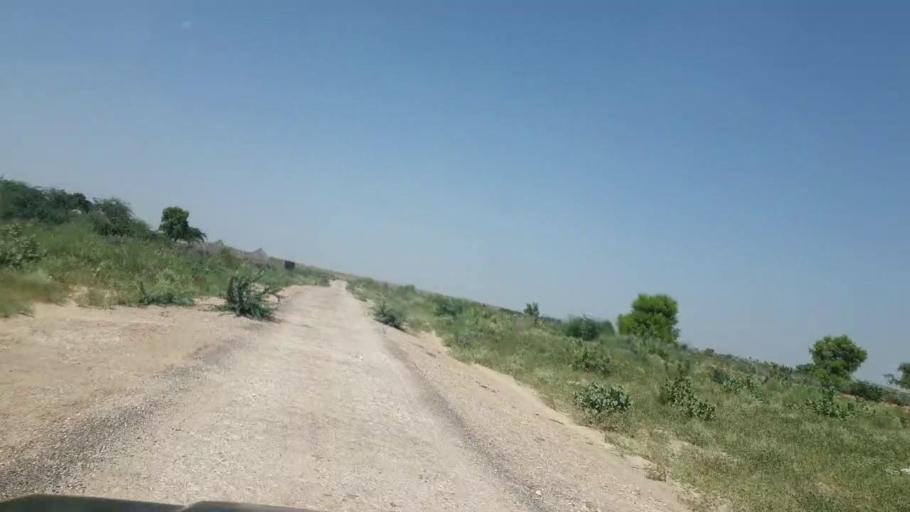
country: PK
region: Sindh
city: Chor
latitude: 25.3683
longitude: 70.3209
